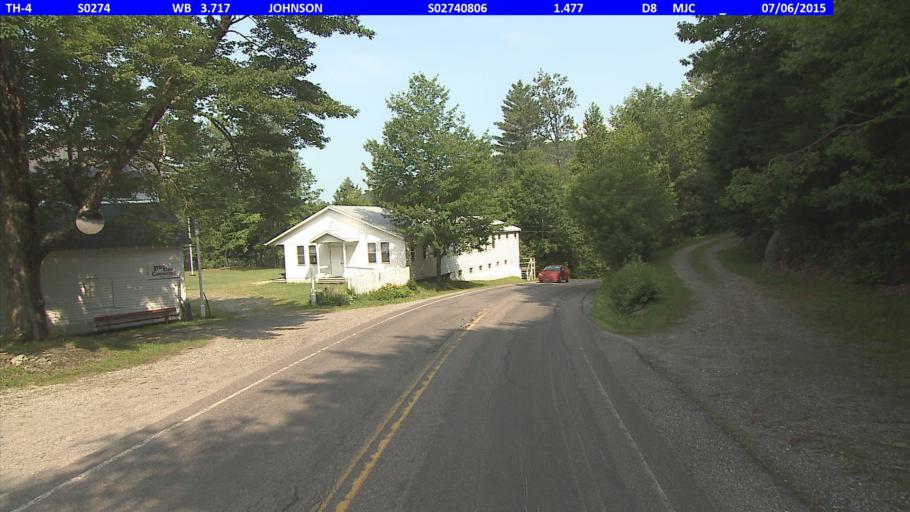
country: US
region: Vermont
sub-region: Lamoille County
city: Johnson
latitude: 44.6490
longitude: -72.7248
